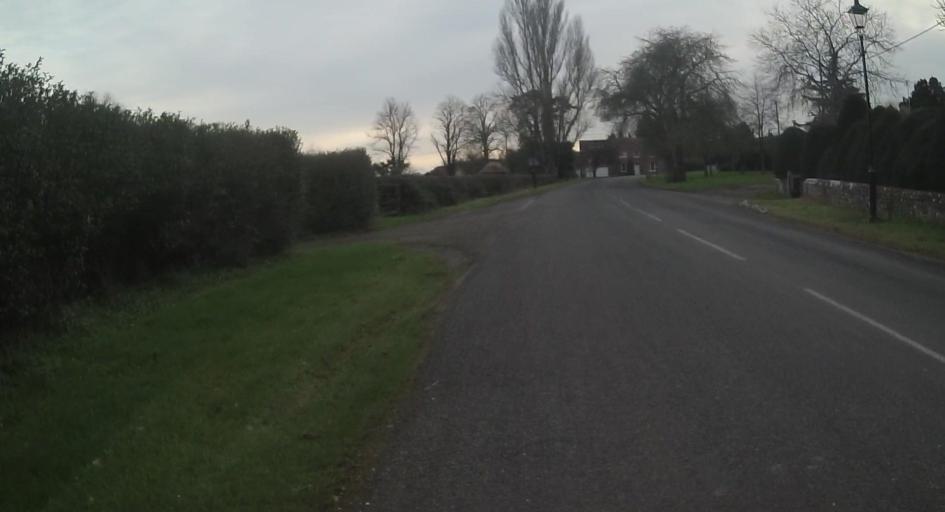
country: GB
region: England
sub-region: Hampshire
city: Overton
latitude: 51.2163
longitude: -1.3743
